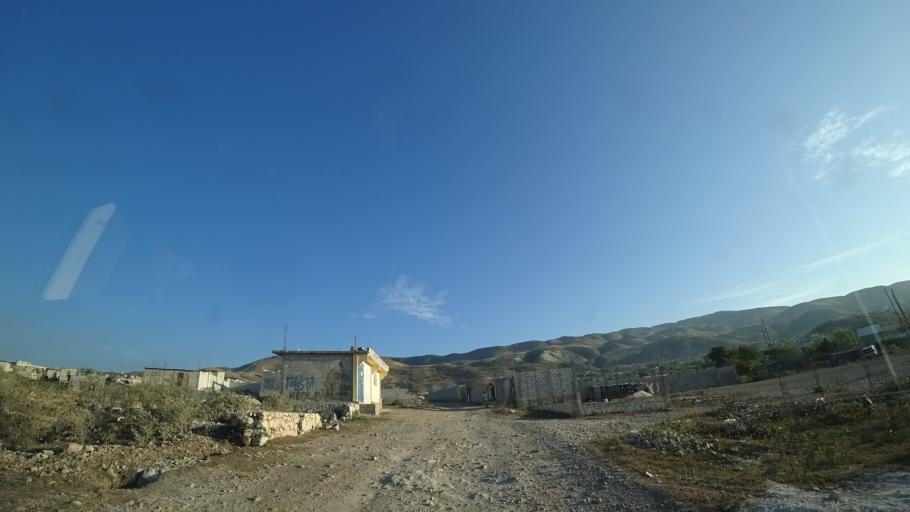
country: HT
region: Ouest
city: Cabaret
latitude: 18.6862
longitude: -72.3175
